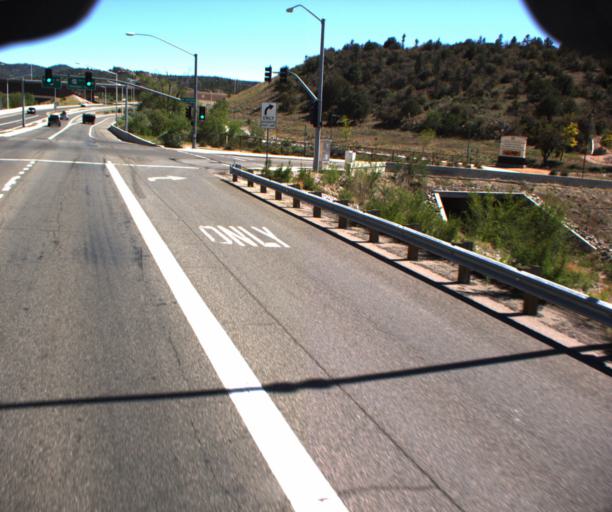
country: US
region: Arizona
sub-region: Yavapai County
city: Prescott
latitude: 34.5512
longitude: -112.4500
